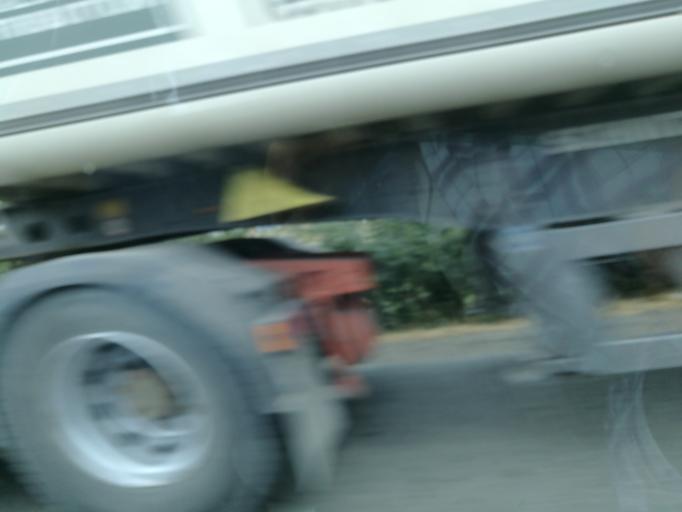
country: RO
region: Braila
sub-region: Municipiul Braila
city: Braila
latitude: 45.2873
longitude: 28.0027
